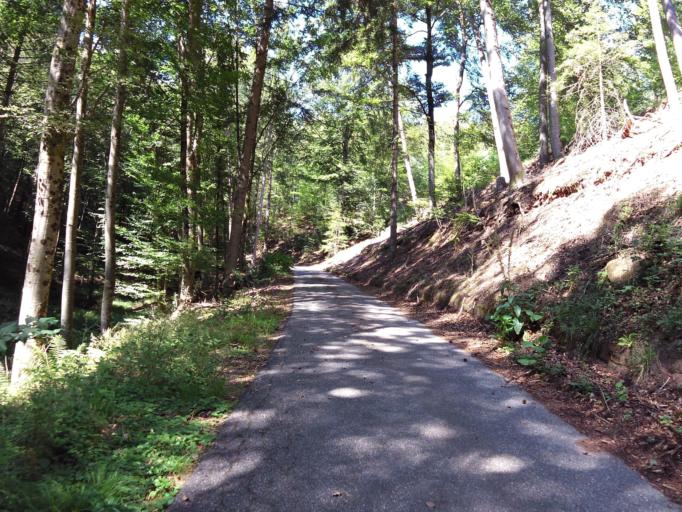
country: DE
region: Rheinland-Pfalz
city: Elmstein
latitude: 49.3784
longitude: 7.9473
